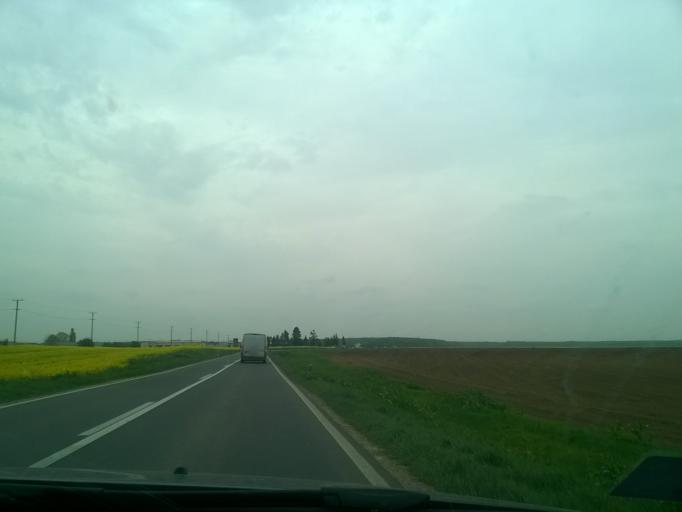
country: RS
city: Hrtkovci
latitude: 44.8531
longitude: 19.7710
